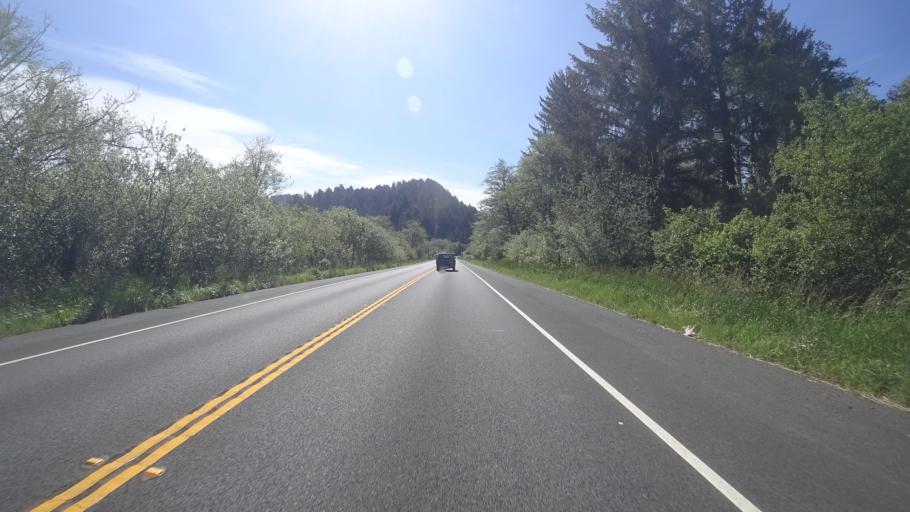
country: US
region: California
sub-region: Del Norte County
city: Bertsch-Oceanview
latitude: 41.5578
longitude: -124.0587
